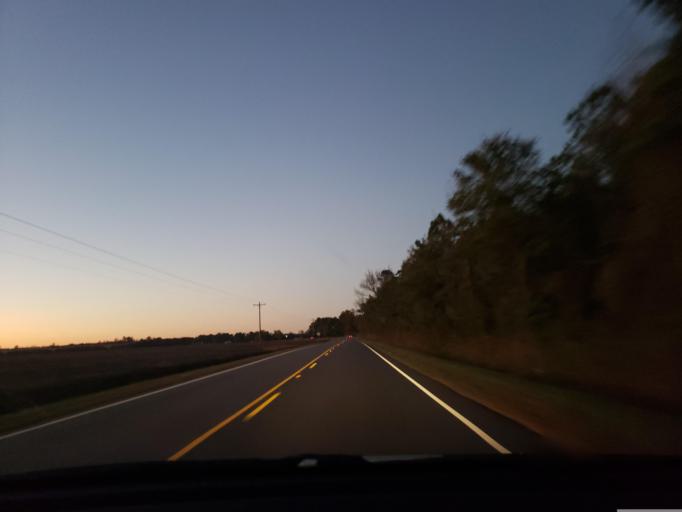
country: US
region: North Carolina
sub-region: Duplin County
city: Kenansville
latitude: 34.9160
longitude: -77.9311
